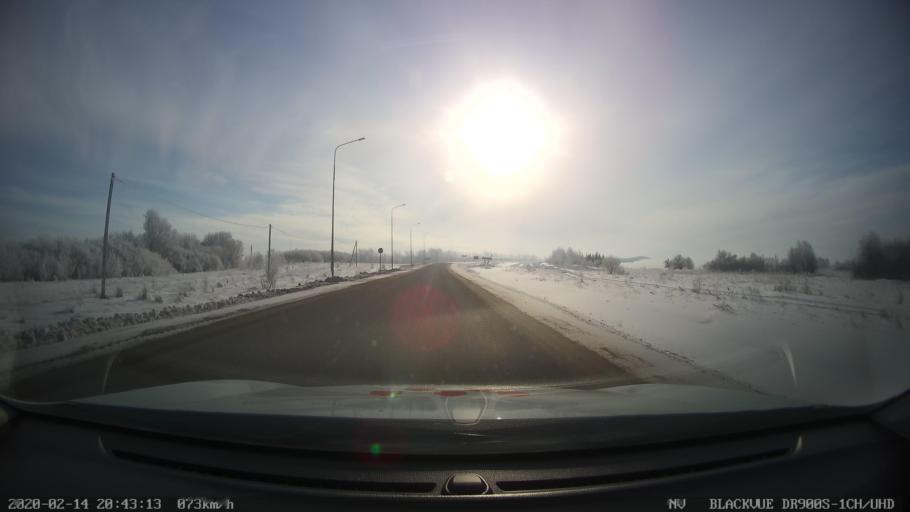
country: RU
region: Tatarstan
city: Kuybyshevskiy Zaton
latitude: 55.3103
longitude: 49.1461
